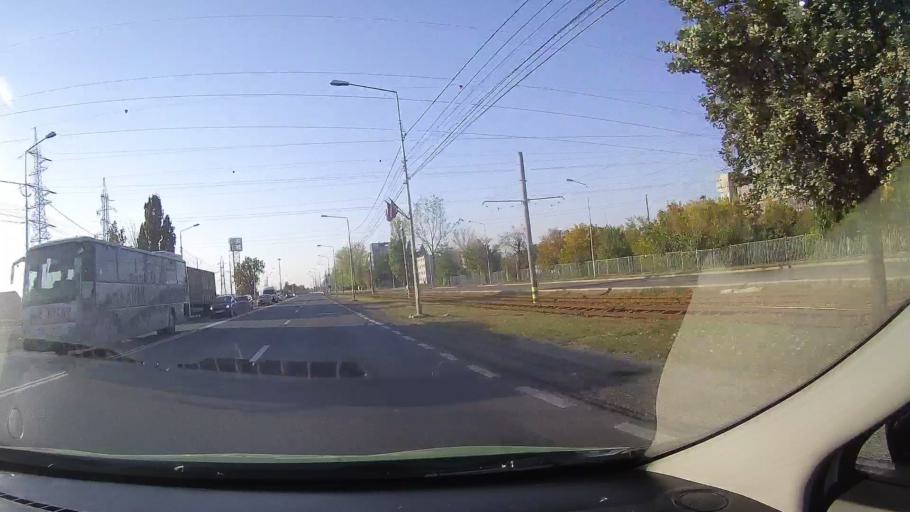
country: RO
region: Bihor
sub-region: Comuna Santandrei
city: Santandrei
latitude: 47.0813
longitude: 21.8918
